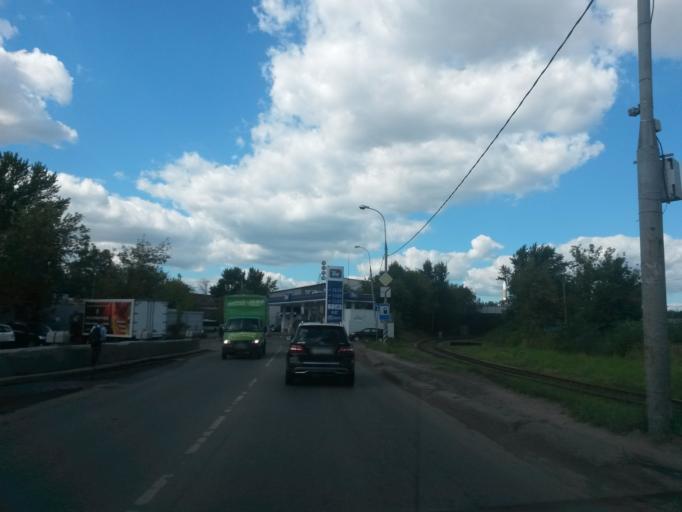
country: RU
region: Moskovskaya
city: Kozhukhovo
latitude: 55.7084
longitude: 37.7022
